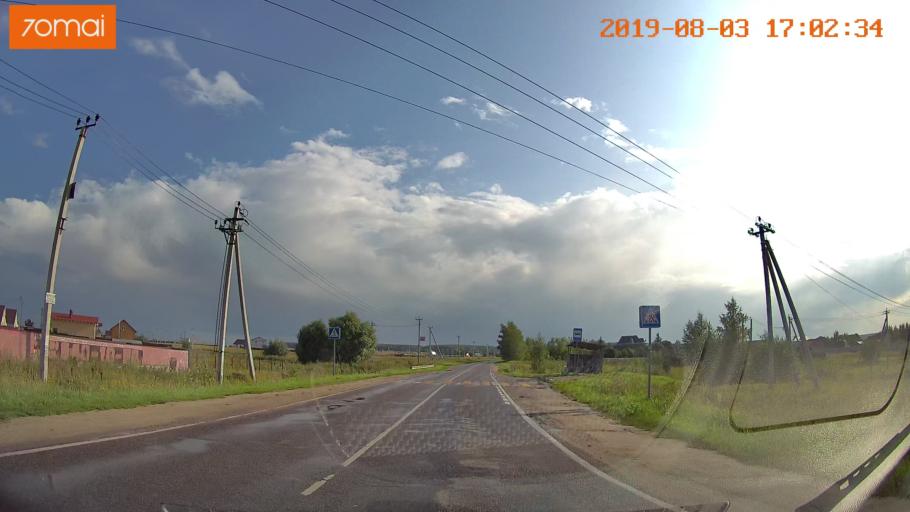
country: RU
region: Moskovskaya
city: Troitskoye
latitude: 55.3451
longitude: 38.5833
